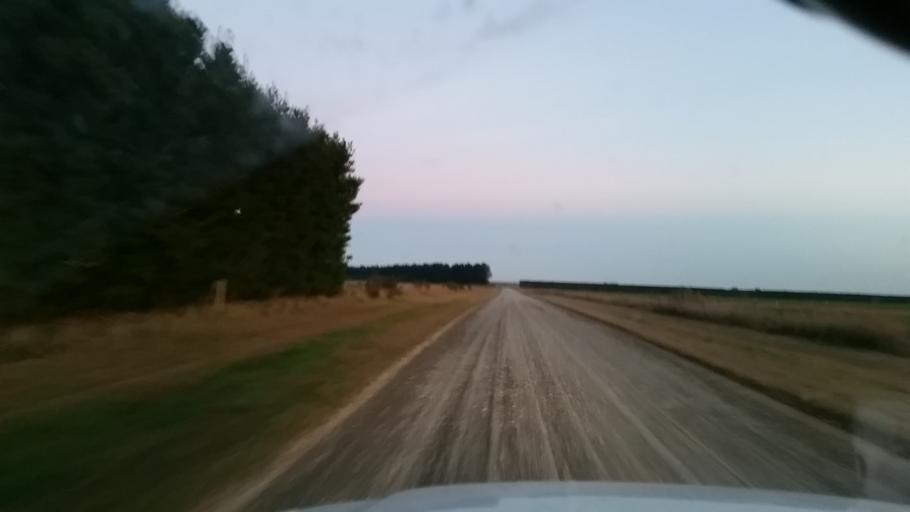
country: NZ
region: Canterbury
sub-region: Ashburton District
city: Tinwald
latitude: -43.9406
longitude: 171.6097
